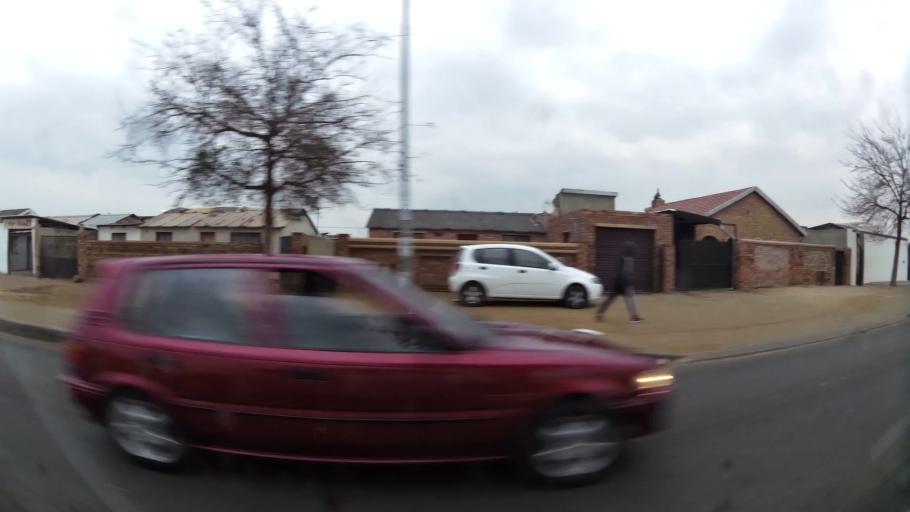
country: ZA
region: Gauteng
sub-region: City of Johannesburg Metropolitan Municipality
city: Soweto
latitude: -26.2501
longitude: 27.8540
